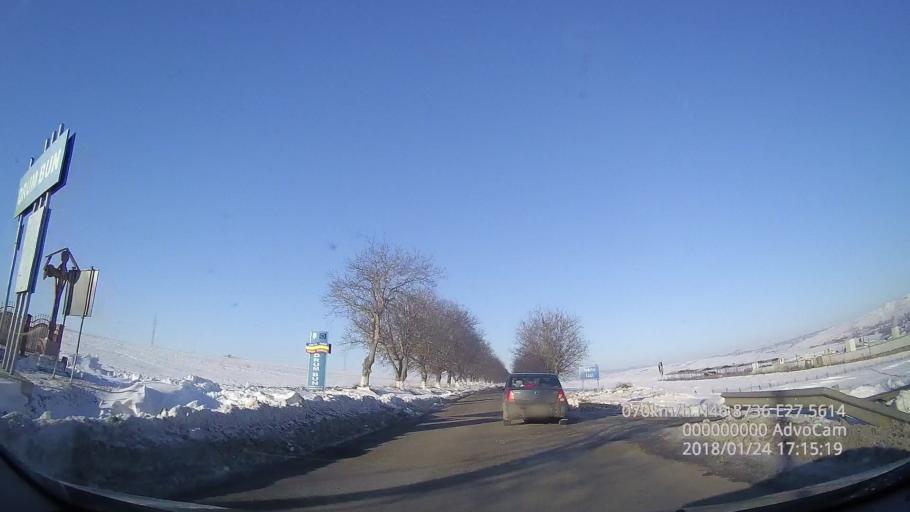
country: RO
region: Vaslui
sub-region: Comuna Rebricea
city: Rebricea
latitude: 46.8742
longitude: 27.5616
